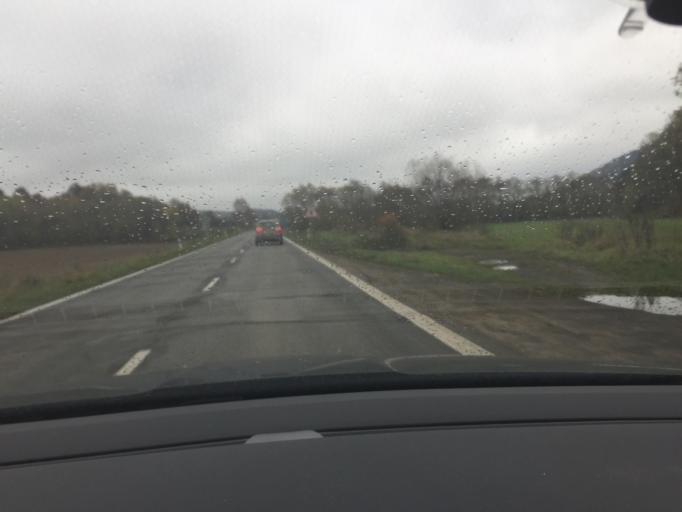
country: SK
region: Presovsky
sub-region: Okres Bardejov
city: Bardejov
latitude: 49.3238
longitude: 21.1452
